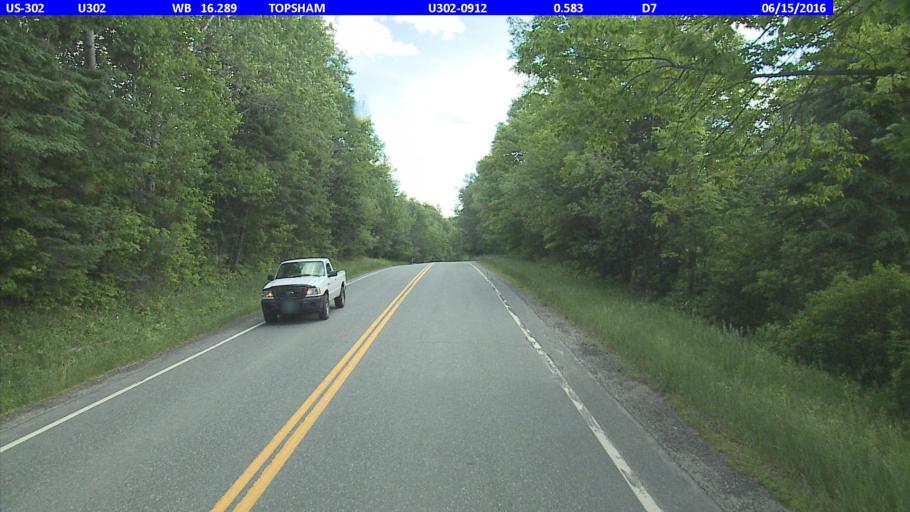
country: US
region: Vermont
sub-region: Washington County
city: South Barre
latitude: 44.1458
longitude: -72.3102
